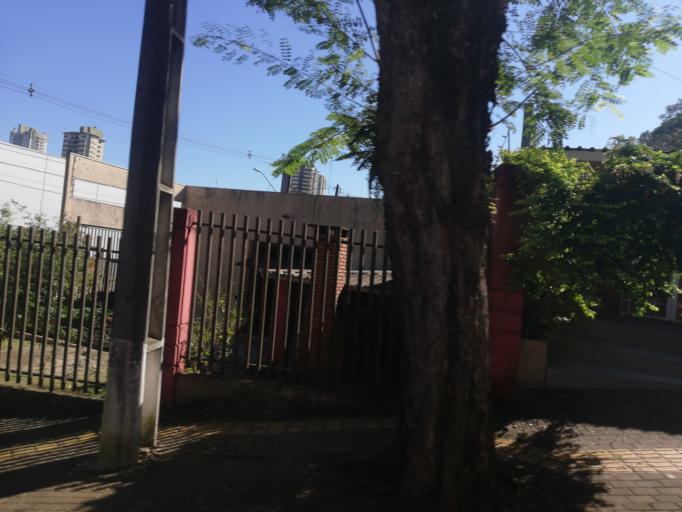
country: BR
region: Parana
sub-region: Foz Do Iguacu
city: Foz do Iguacu
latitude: -25.5468
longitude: -54.5771
